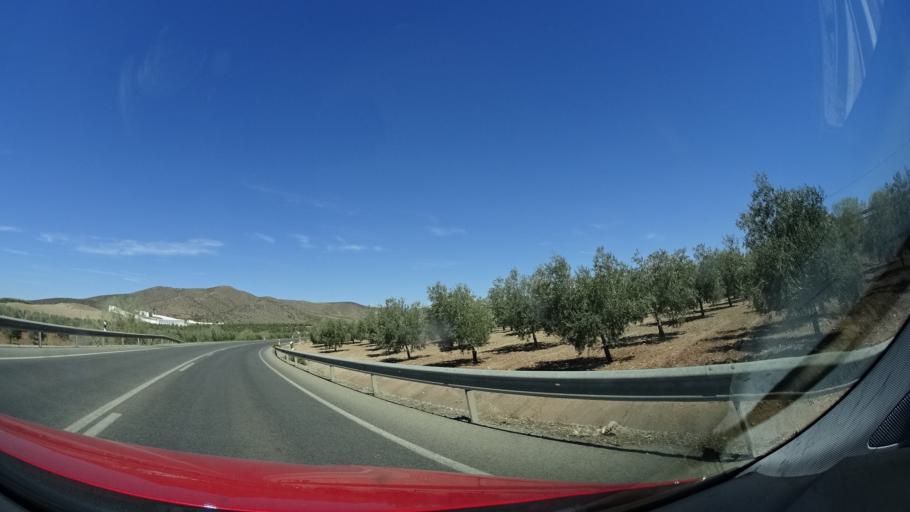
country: ES
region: Andalusia
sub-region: Provincia de Malaga
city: Sierra de Yeguas
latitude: 37.1173
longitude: -4.8795
